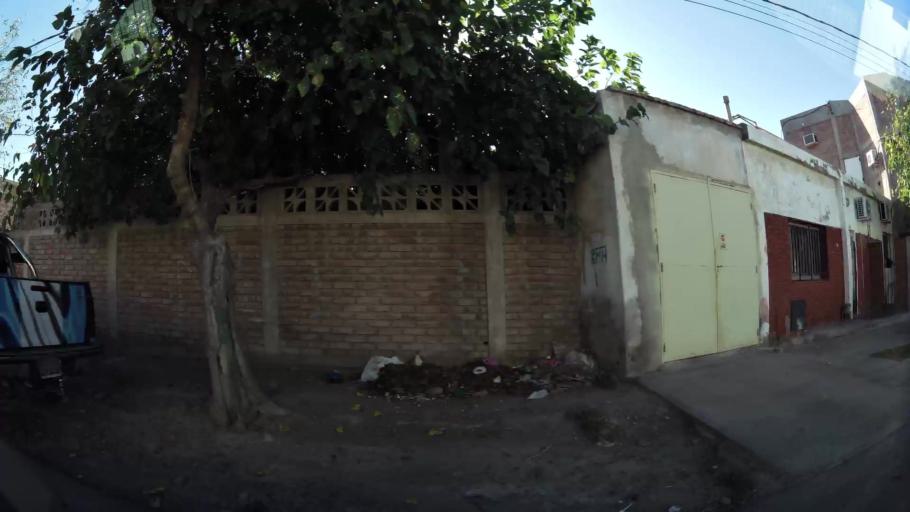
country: AR
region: San Juan
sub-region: Departamento de Santa Lucia
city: Santa Lucia
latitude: -31.5469
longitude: -68.5151
